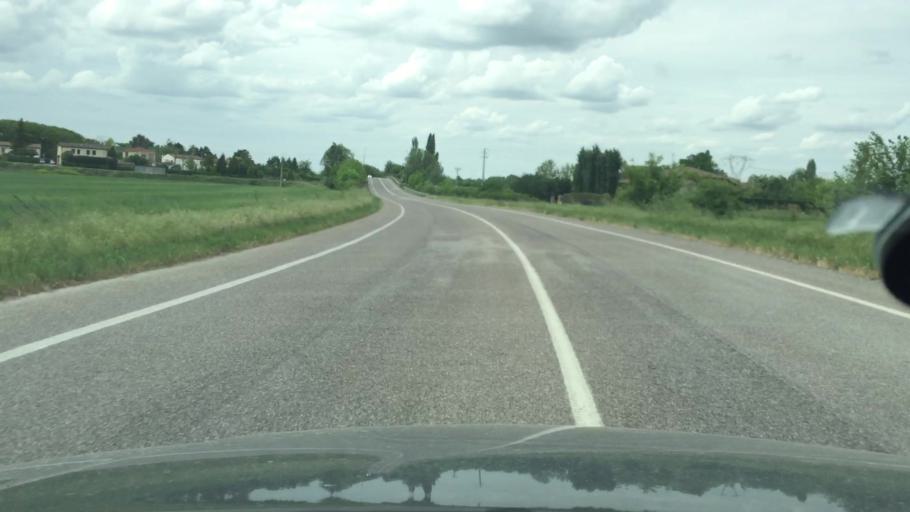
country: IT
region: Emilia-Romagna
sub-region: Provincia di Ferrara
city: Cona
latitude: 44.8098
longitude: 11.7172
